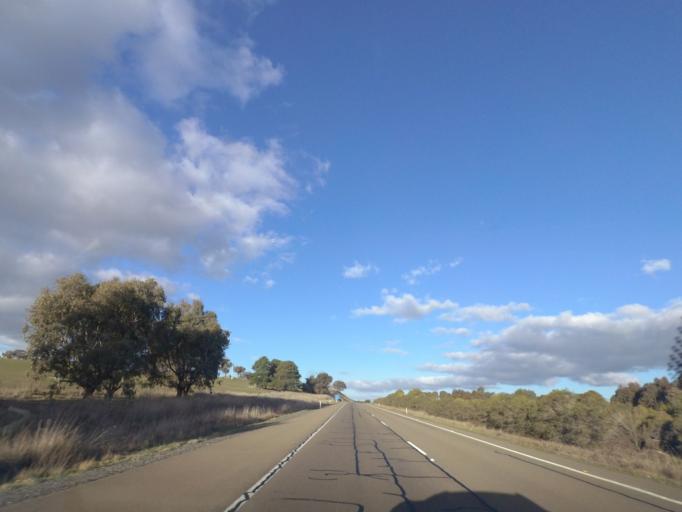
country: AU
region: New South Wales
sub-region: Yass Valley
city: Yass
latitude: -34.8070
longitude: 148.5846
